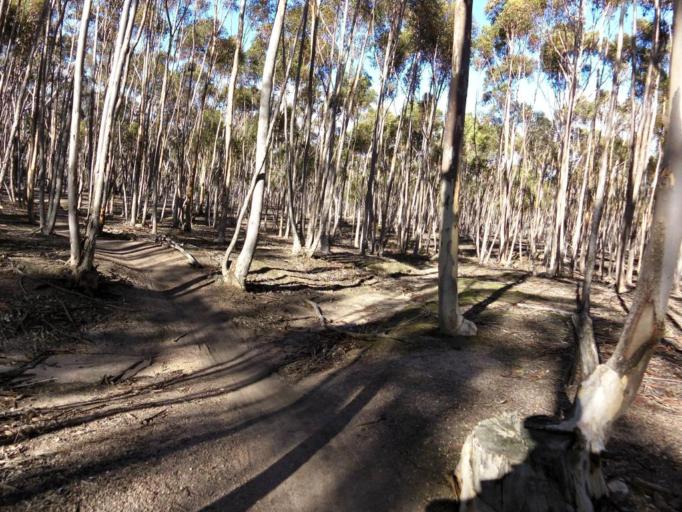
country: AU
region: Victoria
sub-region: Greater Geelong
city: Lara
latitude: -37.9596
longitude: 144.4053
